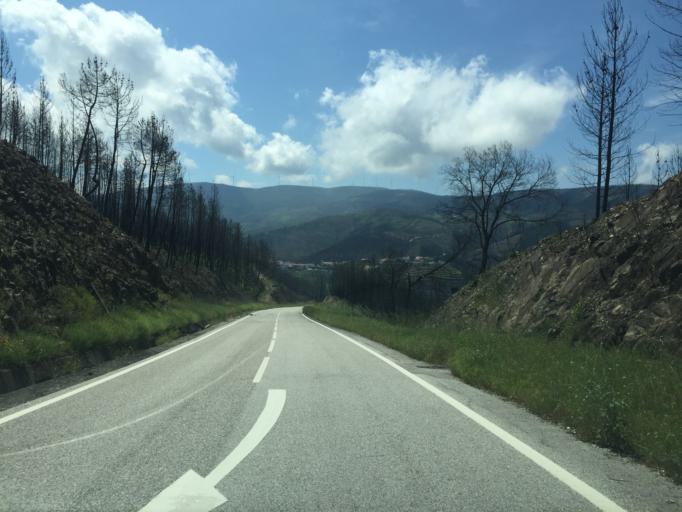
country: PT
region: Coimbra
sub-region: Pampilhosa da Serra
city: Pampilhosa da Serra
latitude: 39.9879
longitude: -7.9681
